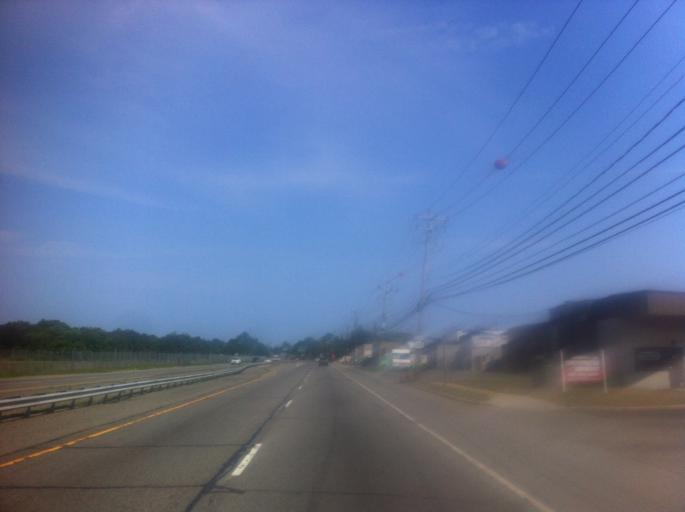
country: US
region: New York
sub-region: Suffolk County
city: East Farmingdale
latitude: 40.7210
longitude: -73.4195
